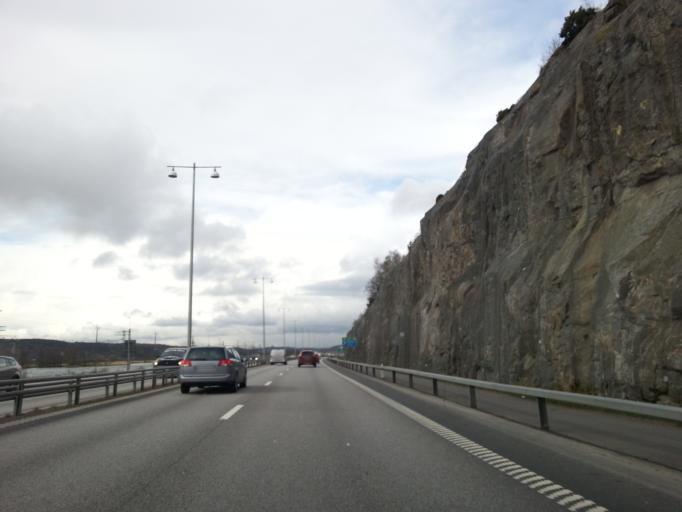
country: SE
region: Vaestra Goetaland
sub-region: Goteborg
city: Gardsten
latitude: 57.8025
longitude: 12.0165
